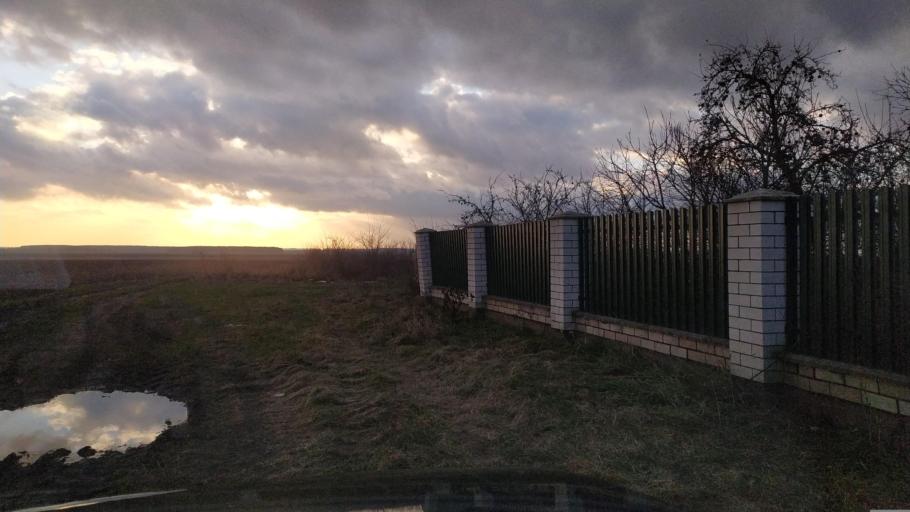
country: BY
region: Brest
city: Kamyanyets
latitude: 52.4243
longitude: 23.7704
